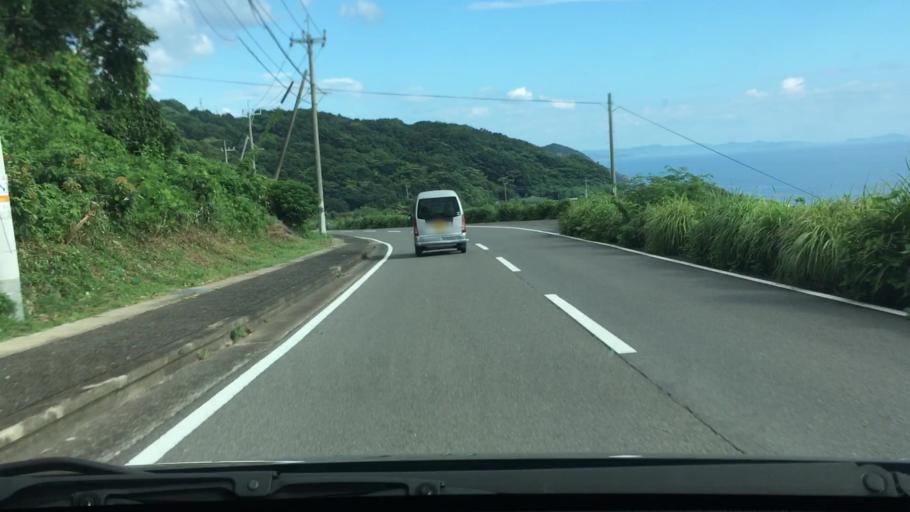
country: JP
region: Nagasaki
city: Togitsu
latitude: 32.8490
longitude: 129.6924
